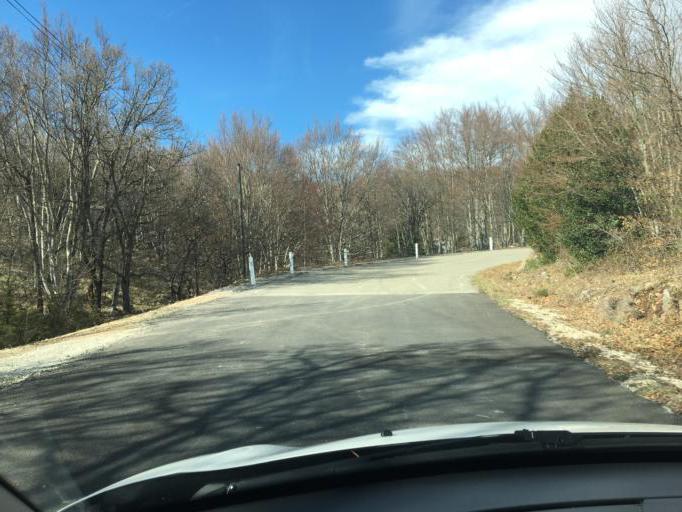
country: FR
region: Provence-Alpes-Cote d'Azur
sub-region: Departement du Vaucluse
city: Saint-Saturnin-les-Apt
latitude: 43.9756
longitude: 5.4618
